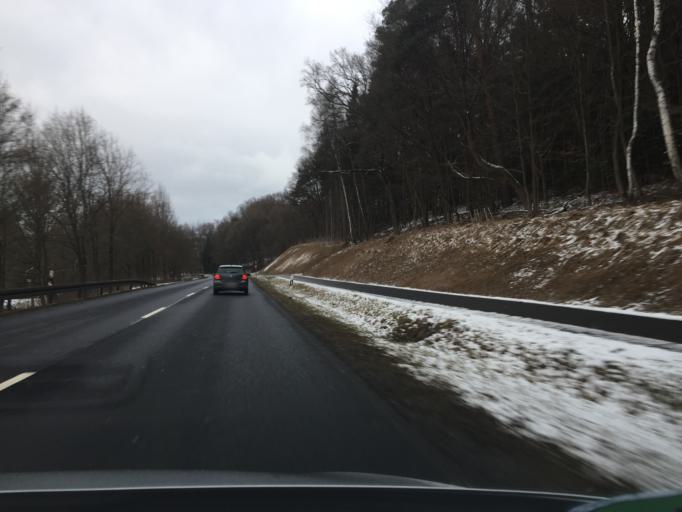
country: DE
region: Bavaria
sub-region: Regierungsbezirk Unterfranken
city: Mombris
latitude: 50.0490
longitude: 9.1954
